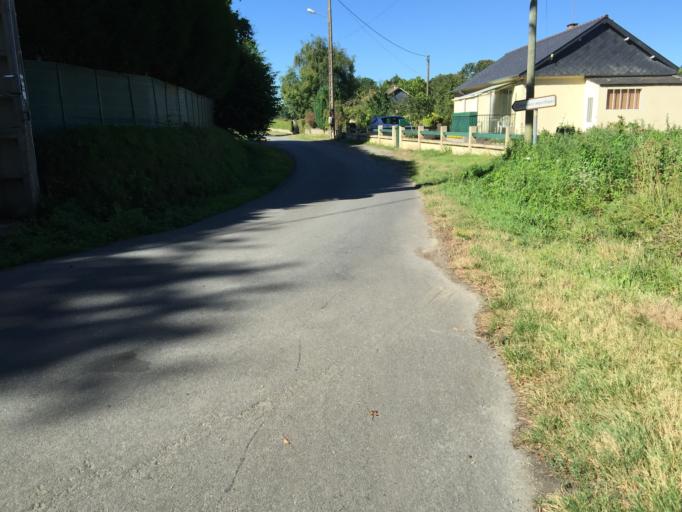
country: FR
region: Brittany
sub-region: Departement des Cotes-d'Armor
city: Pleslin-Trigavou
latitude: 48.5306
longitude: -2.0579
